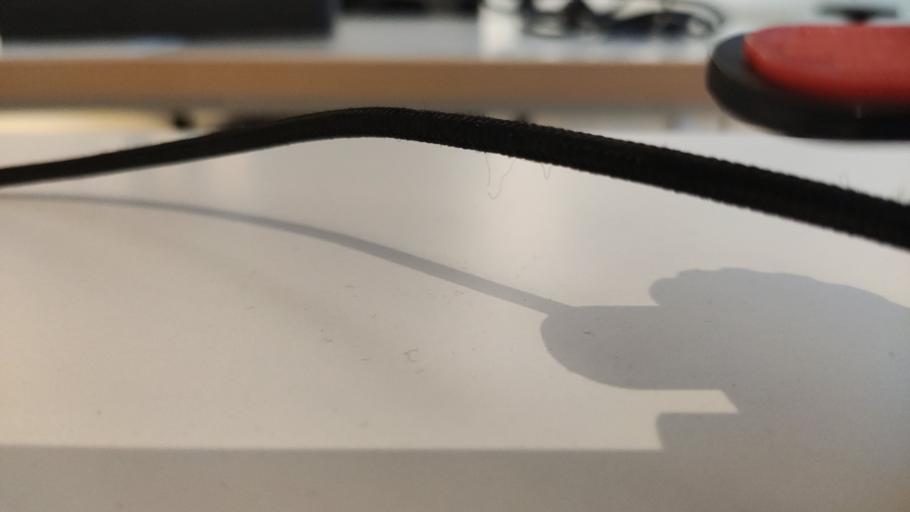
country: RU
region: Moskovskaya
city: Ruza
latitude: 55.7950
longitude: 36.2864
